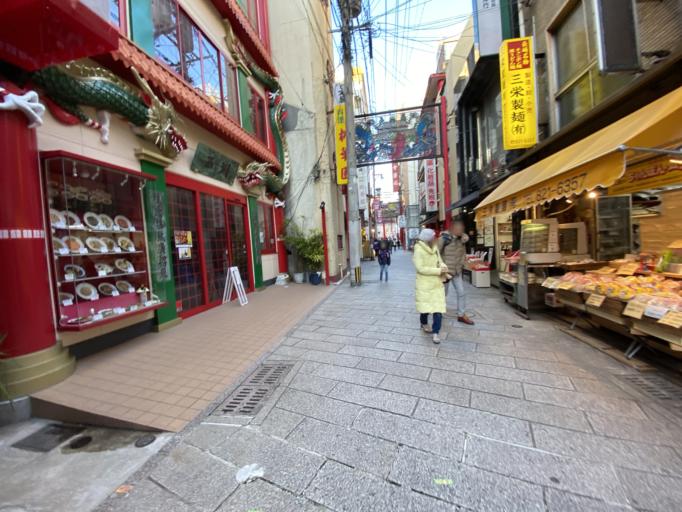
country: JP
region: Nagasaki
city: Nagasaki-shi
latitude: 32.7416
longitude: 129.8754
